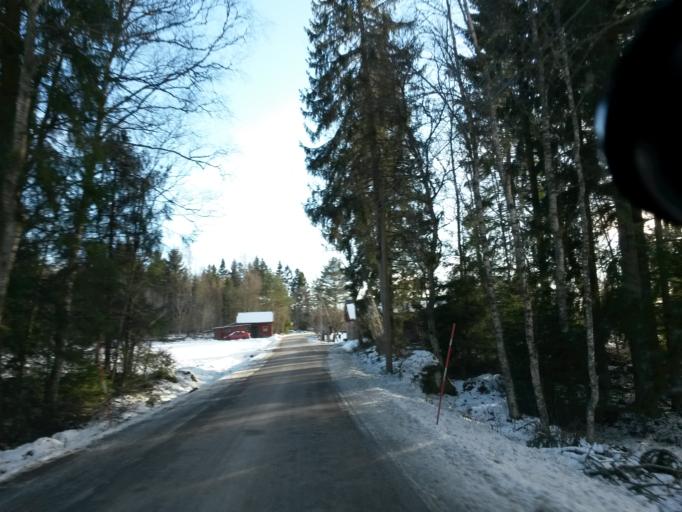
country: SE
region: Vaestra Goetaland
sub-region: Vargarda Kommun
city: Vargarda
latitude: 58.0151
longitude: 12.8919
